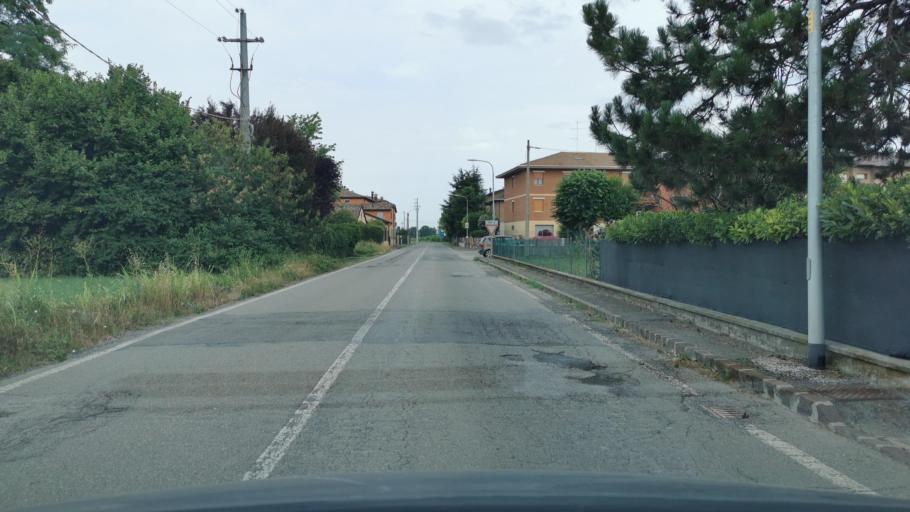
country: IT
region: Emilia-Romagna
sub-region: Provincia di Modena
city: Villanova
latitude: 44.7062
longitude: 10.9009
